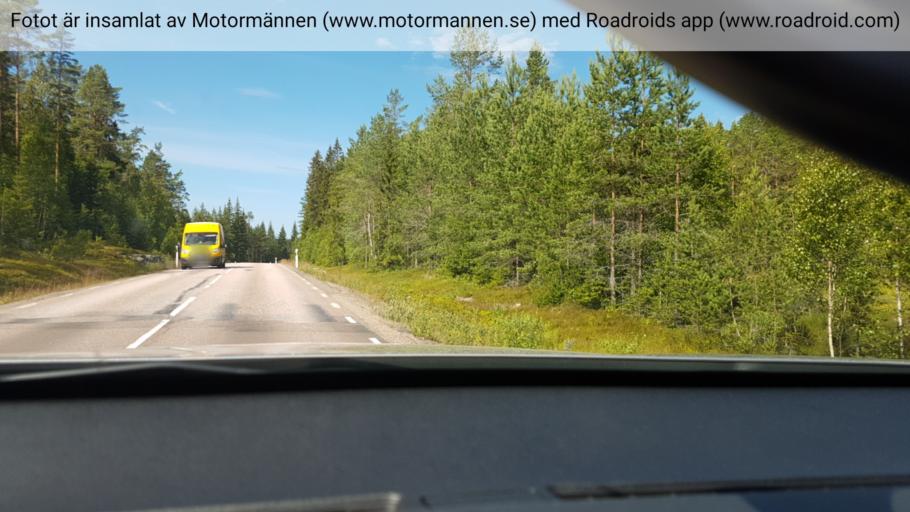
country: SE
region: Vaermland
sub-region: Munkfors Kommun
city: Munkfors
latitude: 59.8751
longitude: 13.3719
